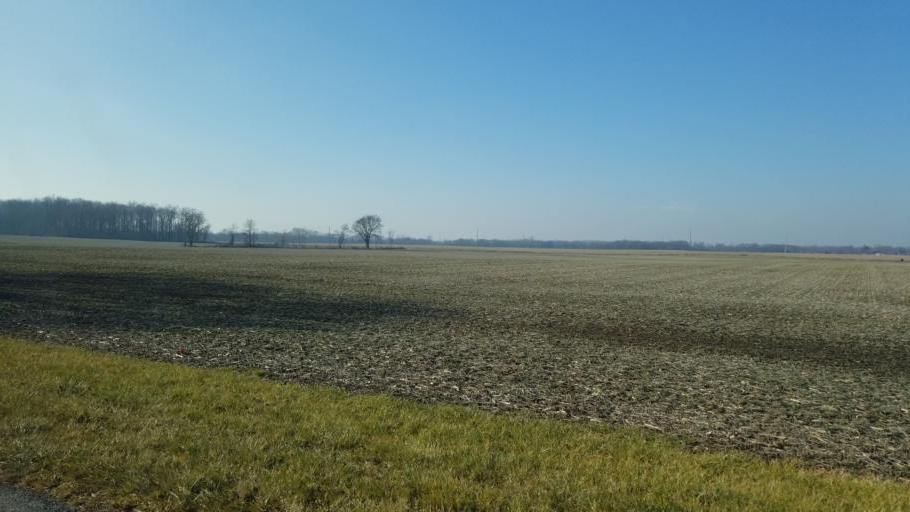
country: US
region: Ohio
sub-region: Seneca County
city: Tiffin
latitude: 41.0797
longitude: -83.1126
